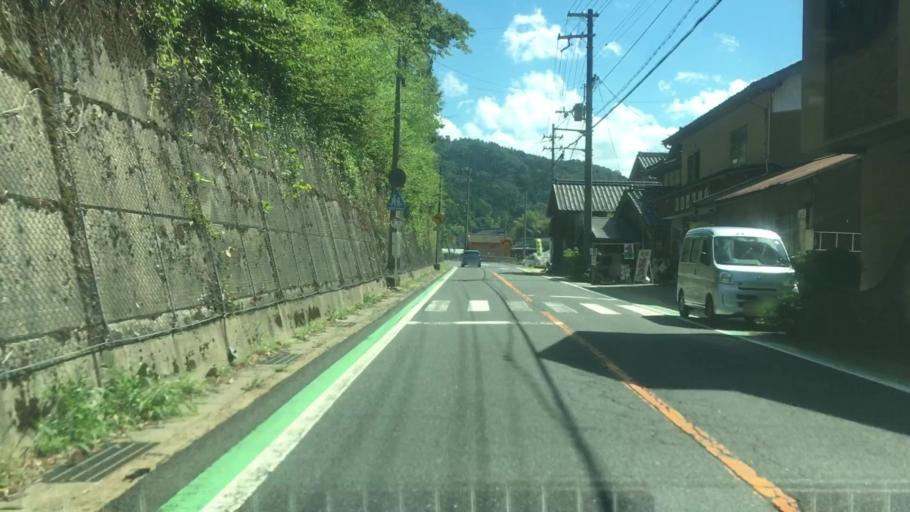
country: JP
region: Hyogo
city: Toyooka
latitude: 35.5954
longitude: 134.9055
